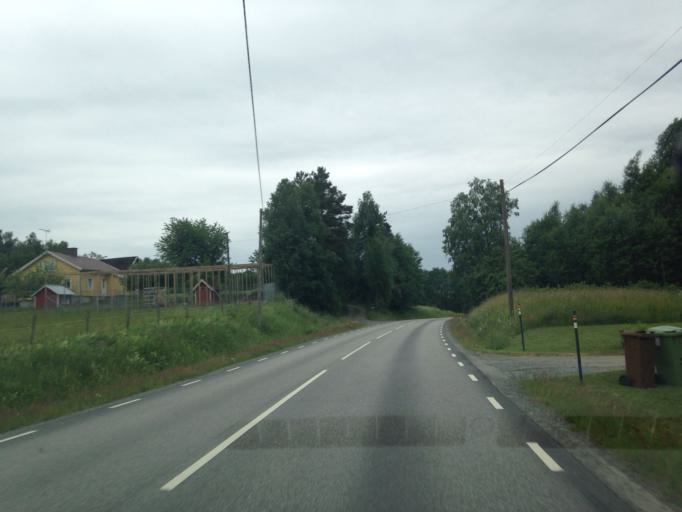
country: SE
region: Vaestra Goetaland
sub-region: Marks Kommun
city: Bua
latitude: 57.4967
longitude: 12.5365
